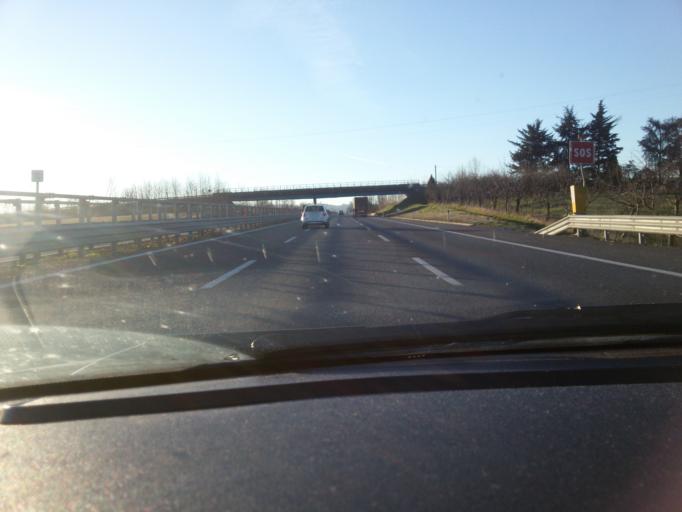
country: IT
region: Piedmont
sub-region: Provincia di Alessandria
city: Mirabello Monferrato
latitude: 45.0398
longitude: 8.5292
